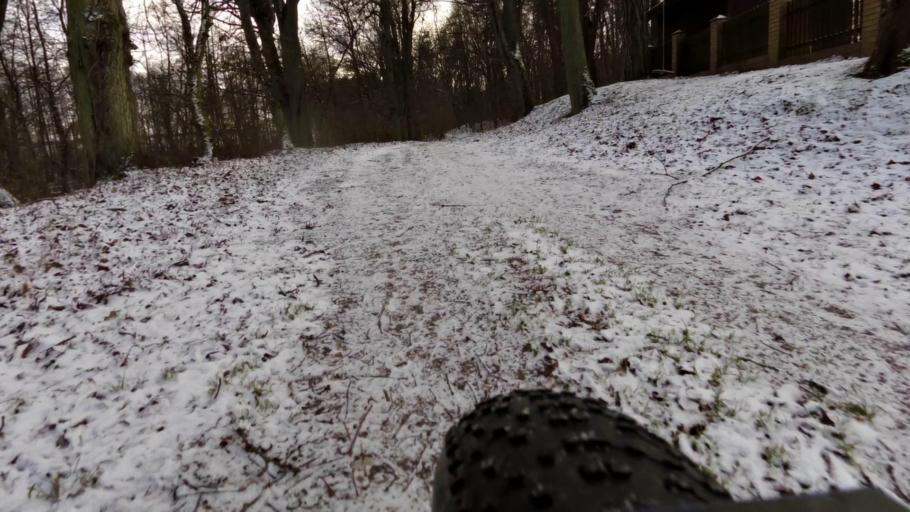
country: PL
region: West Pomeranian Voivodeship
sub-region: Powiat walecki
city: Tuczno
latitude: 53.3035
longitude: 16.2728
